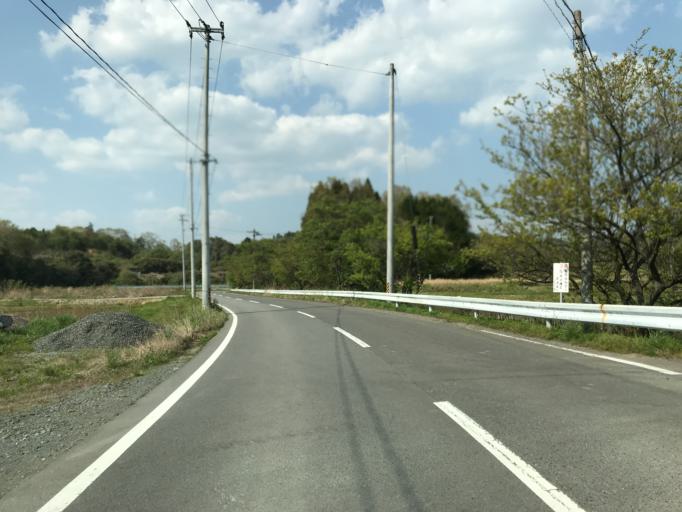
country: JP
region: Fukushima
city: Iwaki
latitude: 36.9656
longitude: 140.7568
